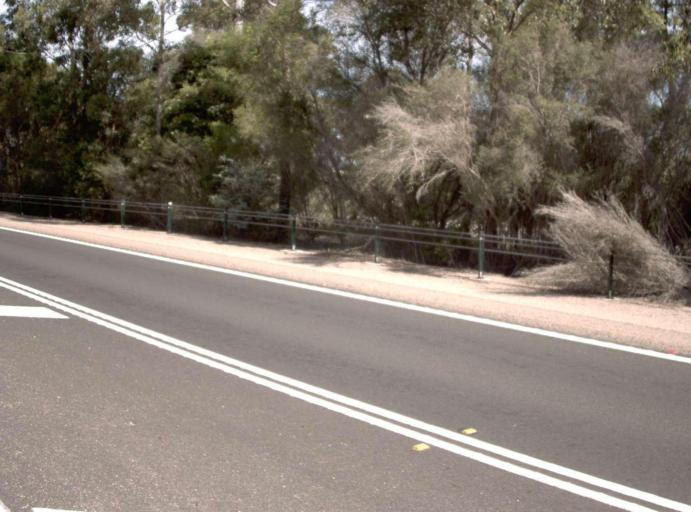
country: AU
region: Victoria
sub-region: East Gippsland
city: Lakes Entrance
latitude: -37.8395
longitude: 147.9241
